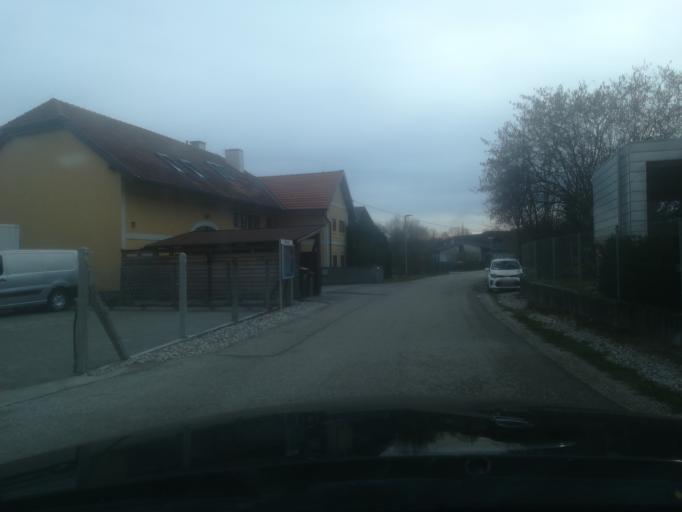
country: AT
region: Upper Austria
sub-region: Wels-Land
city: Gunskirchen
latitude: 48.1086
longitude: 13.9404
